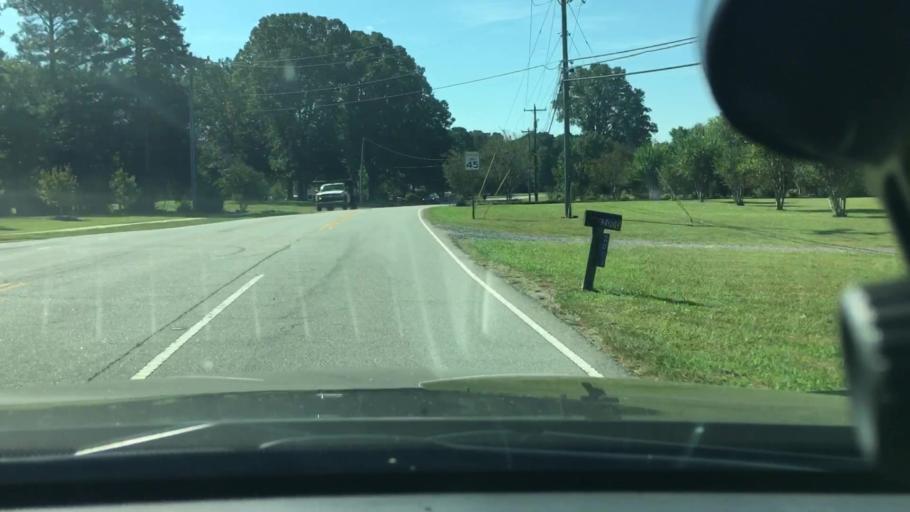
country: US
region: North Carolina
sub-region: Gaston County
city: Mount Holly
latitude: 35.2646
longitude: -80.9754
